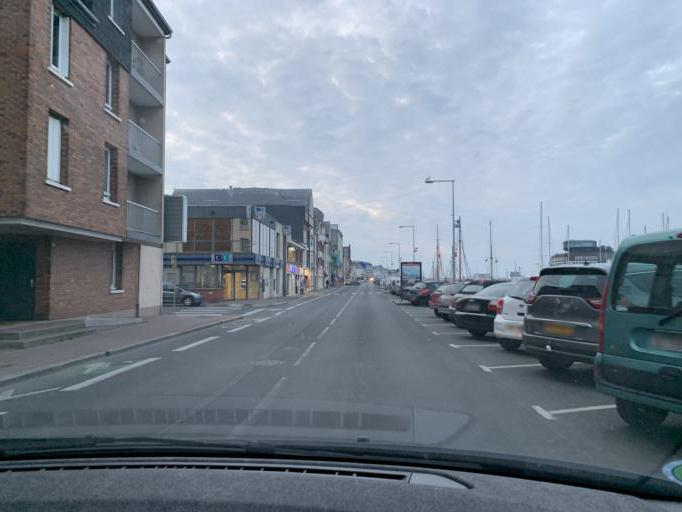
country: FR
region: Haute-Normandie
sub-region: Departement de la Seine-Maritime
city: Fecamp
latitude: 49.7594
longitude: 0.3721
